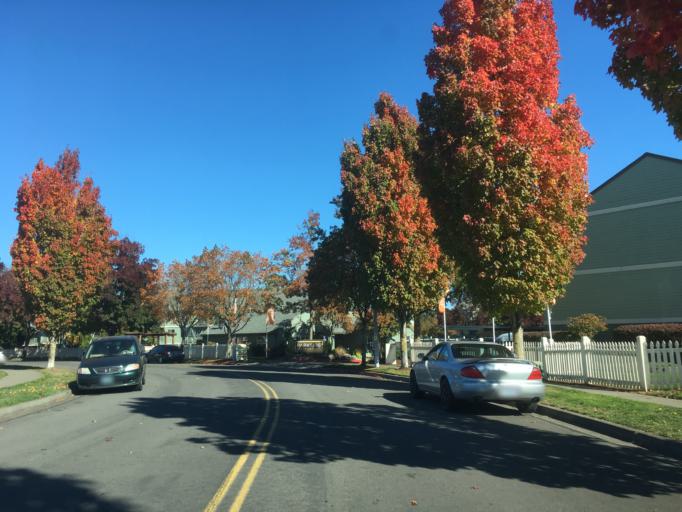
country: US
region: Oregon
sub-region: Multnomah County
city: Gresham
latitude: 45.4875
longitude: -122.4052
